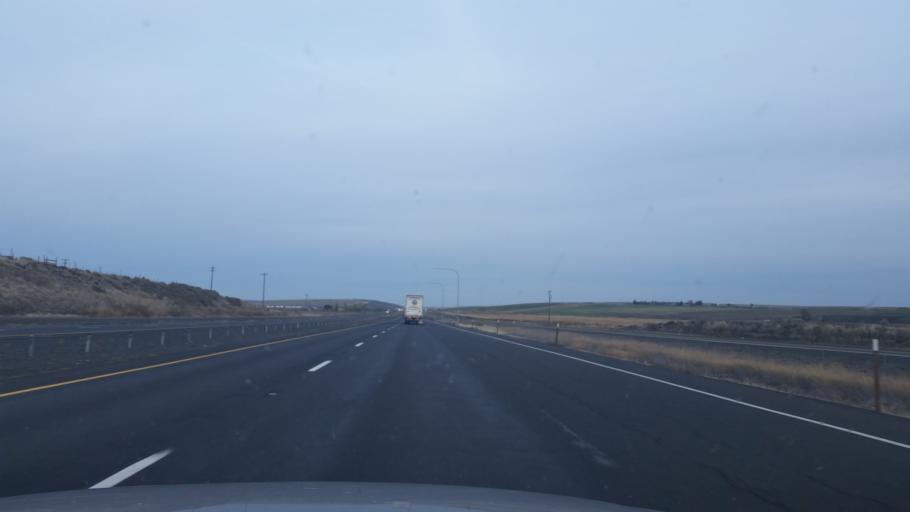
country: US
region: Washington
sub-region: Grant County
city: Warden
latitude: 47.0855
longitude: -119.0396
